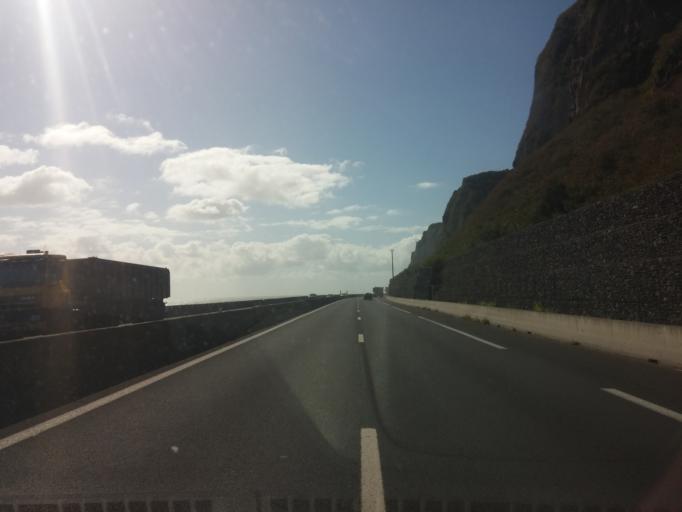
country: RE
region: Reunion
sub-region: Reunion
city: Saint-Denis
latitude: -20.8805
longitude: 55.4001
